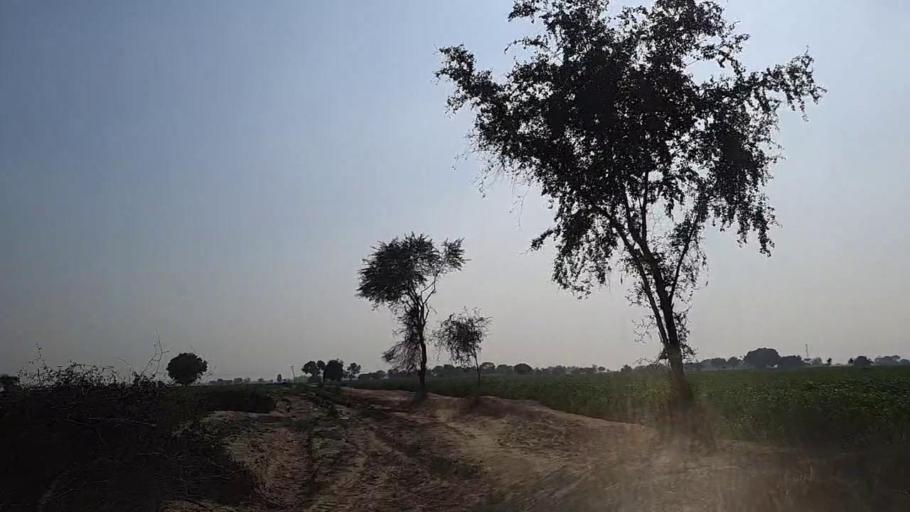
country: PK
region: Sindh
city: Moro
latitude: 26.6807
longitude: 67.9274
